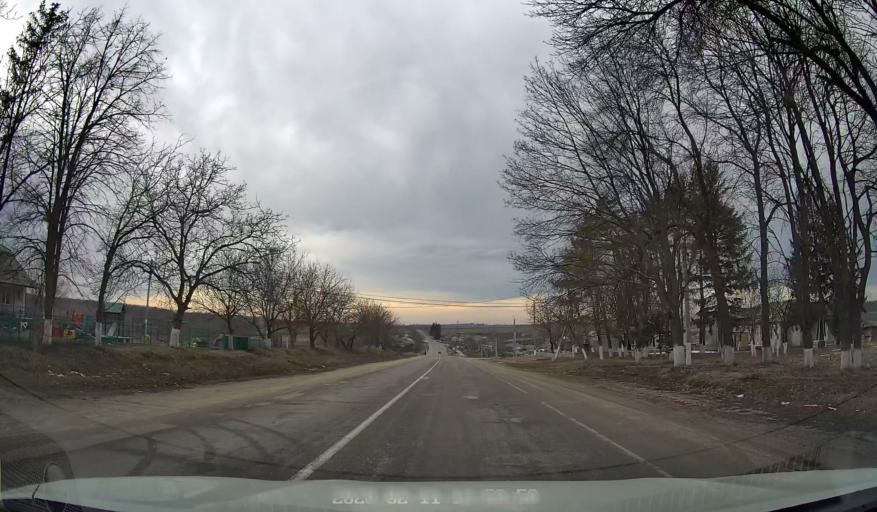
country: MD
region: Briceni
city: Briceni
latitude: 48.3273
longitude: 27.0270
